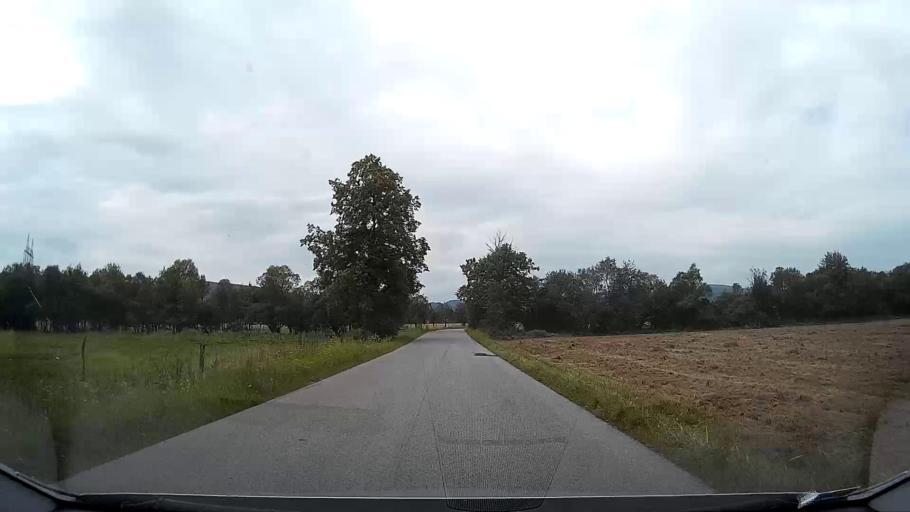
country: SK
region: Presovsky
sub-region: Okres Poprad
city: Poprad
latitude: 48.9870
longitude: 20.3793
